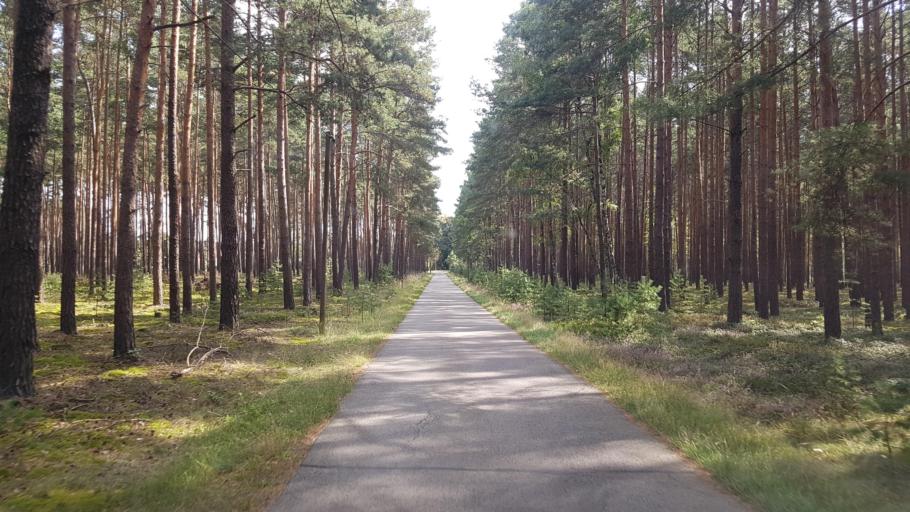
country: DE
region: Brandenburg
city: Hohenbucko
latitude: 51.7533
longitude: 13.5490
